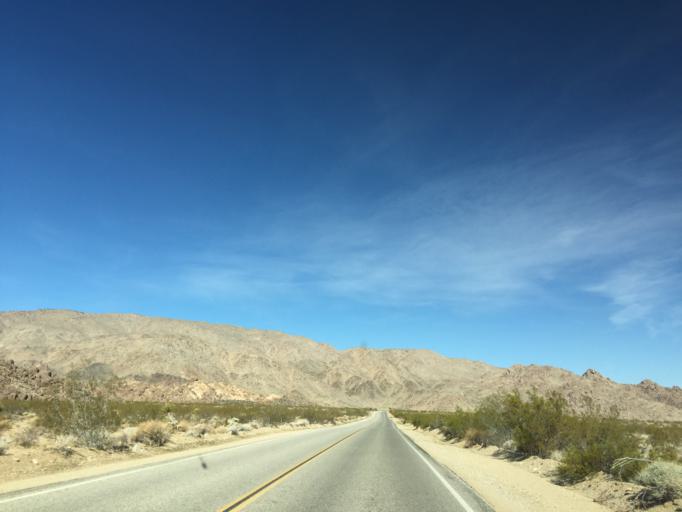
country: US
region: California
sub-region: San Bernardino County
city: Twentynine Palms
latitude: 34.0701
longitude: -116.0272
